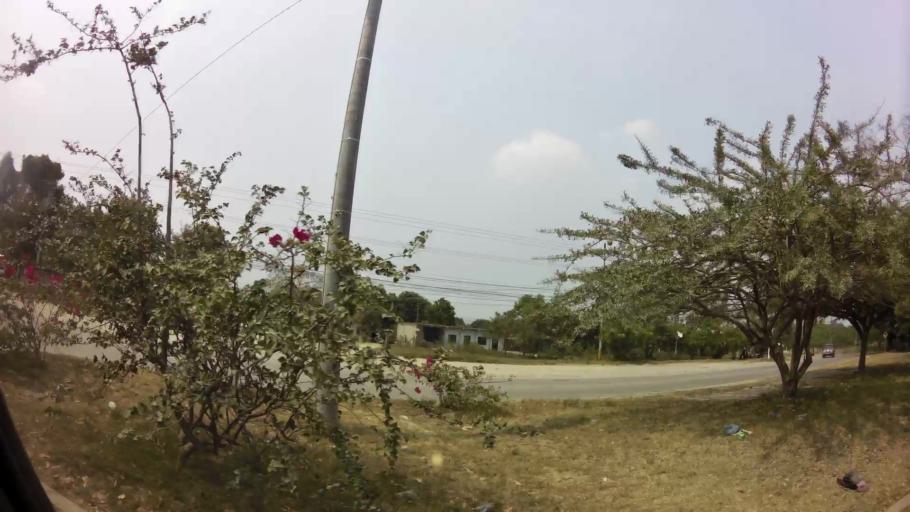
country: HN
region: Cortes
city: La Lima
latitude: 15.4365
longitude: -87.9050
